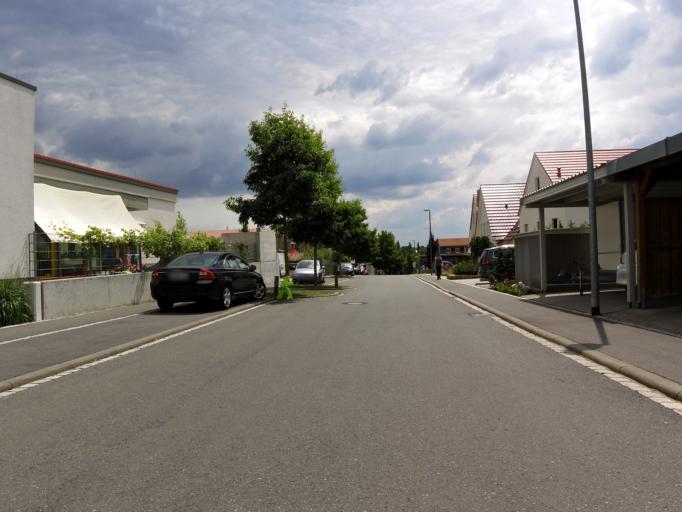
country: DE
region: Bavaria
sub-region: Regierungsbezirk Unterfranken
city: Eibelstadt
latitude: 49.7245
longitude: 9.9650
